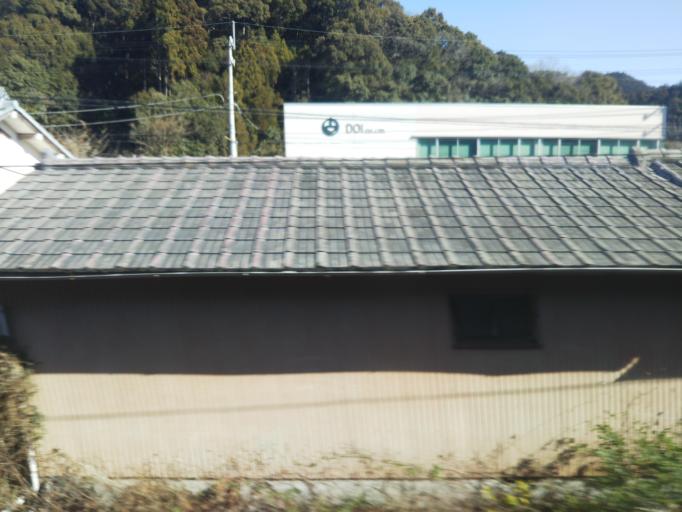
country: JP
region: Kochi
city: Nakamura
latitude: 33.1060
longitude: 133.0987
